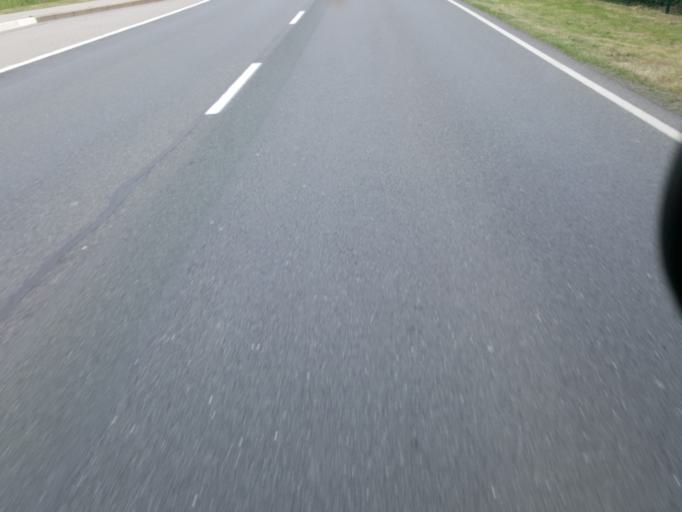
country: DE
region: Lower Saxony
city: Leese
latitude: 52.4936
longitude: 9.1220
